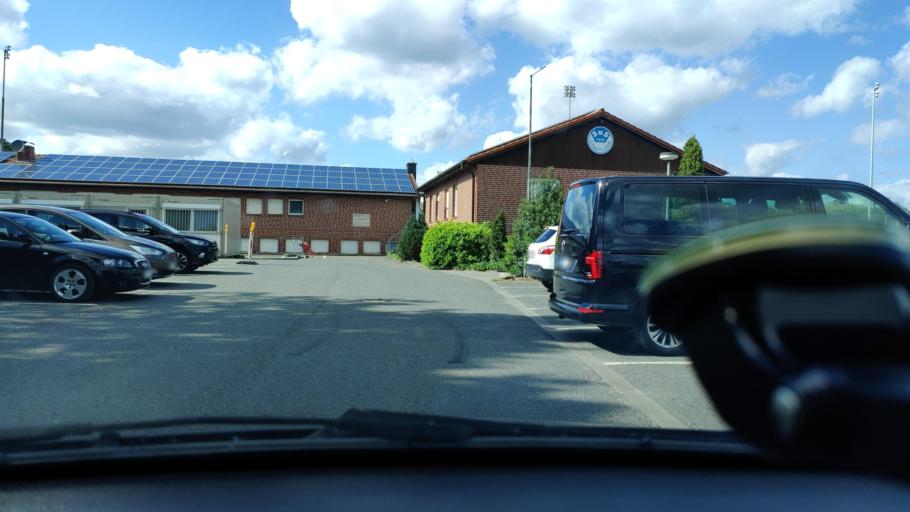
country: DE
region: North Rhine-Westphalia
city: Stadtlohn
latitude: 51.9995
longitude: 6.9289
